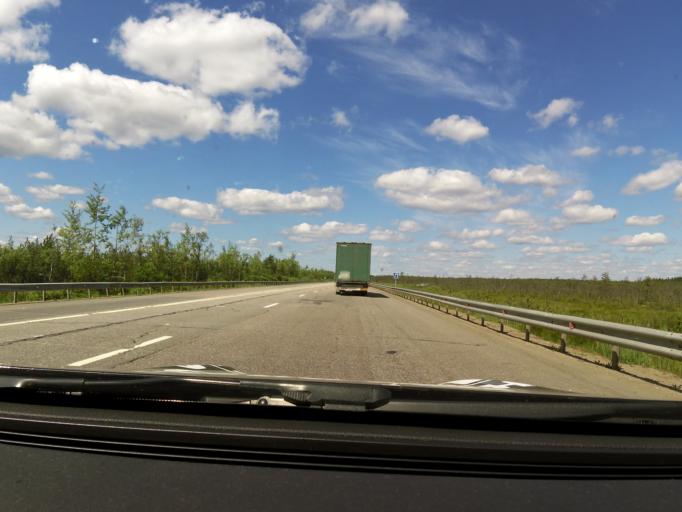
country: RU
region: Tverskaya
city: Kuzhenkino
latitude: 57.7712
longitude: 33.9309
